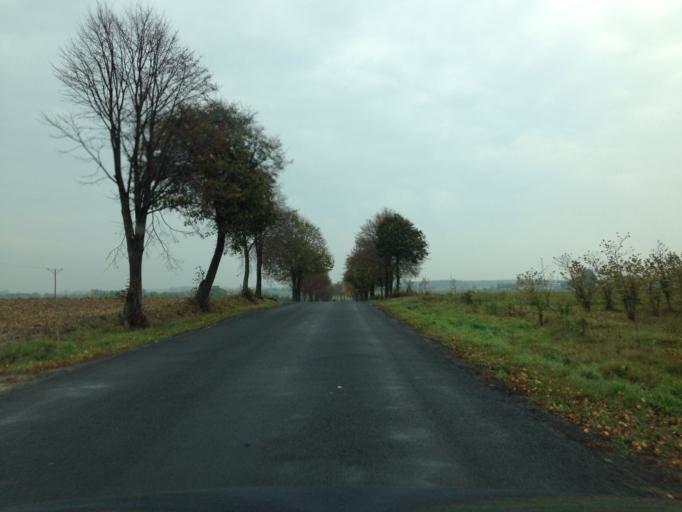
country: PL
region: Kujawsko-Pomorskie
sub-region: Powiat brodnicki
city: Swiedziebnia
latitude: 53.1615
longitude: 19.5761
